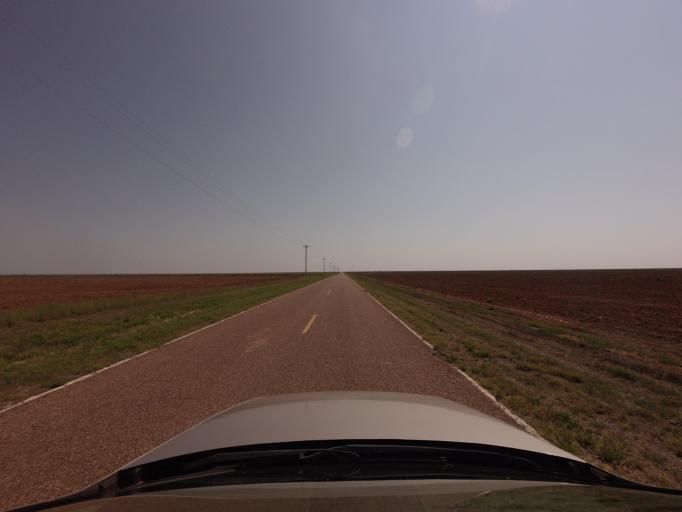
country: US
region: New Mexico
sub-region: Curry County
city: Cannon Air Force Base
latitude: 34.6327
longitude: -103.3128
